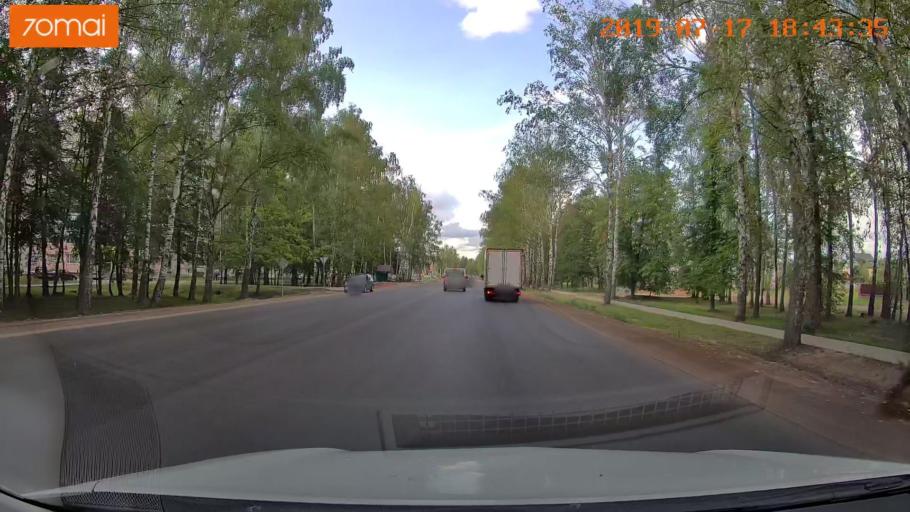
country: BY
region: Mogilev
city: Asipovichy
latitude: 53.3154
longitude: 28.6435
